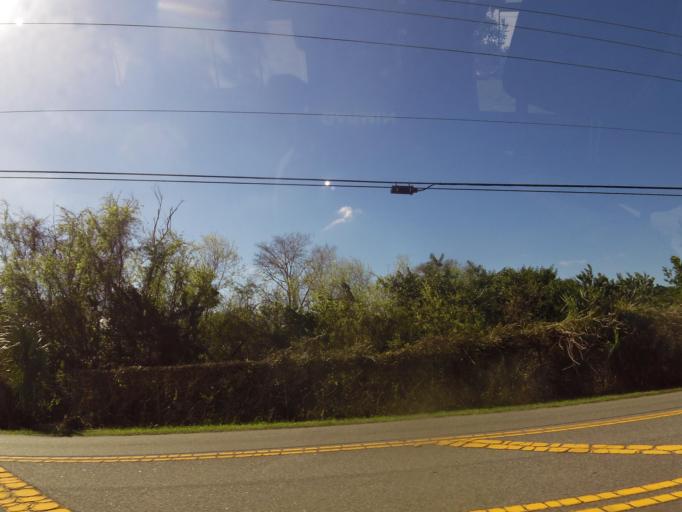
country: US
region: Florida
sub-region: Brevard County
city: Titusville
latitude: 28.5516
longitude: -80.8064
